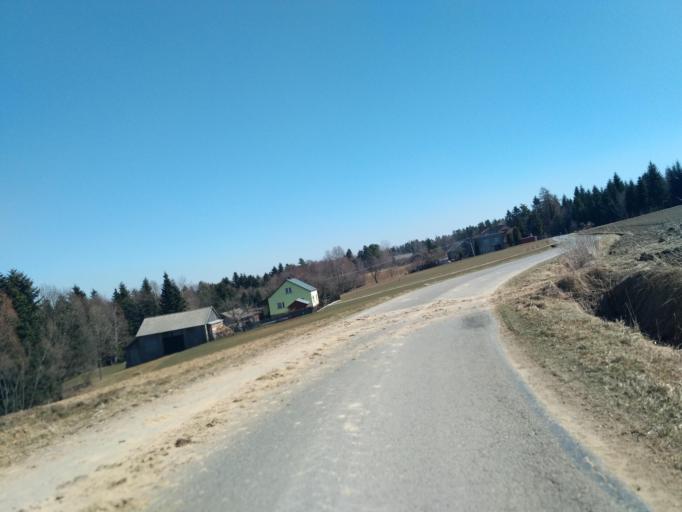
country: PL
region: Subcarpathian Voivodeship
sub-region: Powiat ropczycko-sedziszowski
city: Niedzwiada
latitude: 49.9525
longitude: 21.4898
